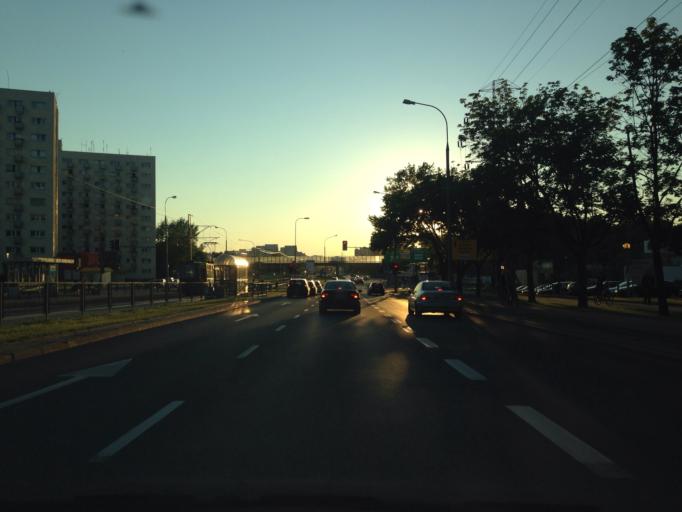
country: PL
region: Masovian Voivodeship
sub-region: Warszawa
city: Zoliborz
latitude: 52.2667
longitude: 20.9636
